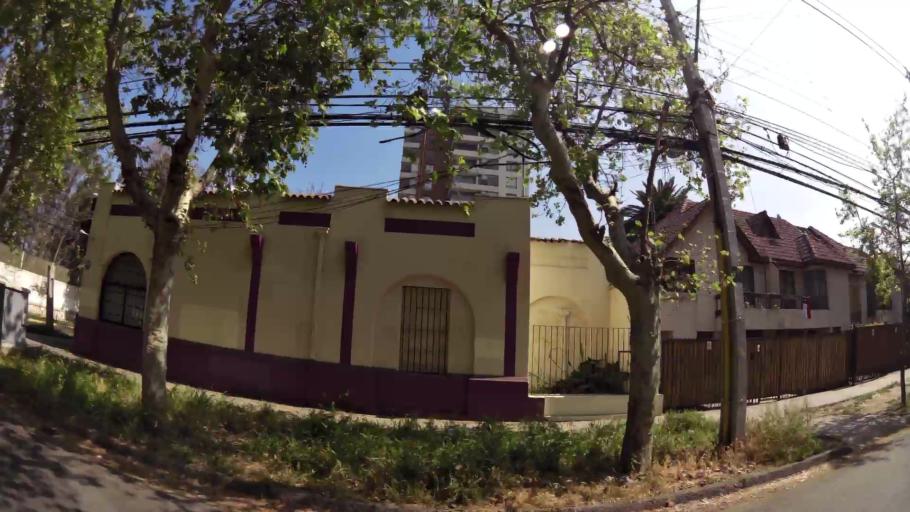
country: CL
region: Santiago Metropolitan
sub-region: Provincia de Santiago
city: Villa Presidente Frei, Nunoa, Santiago, Chile
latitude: -33.4512
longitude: -70.6037
